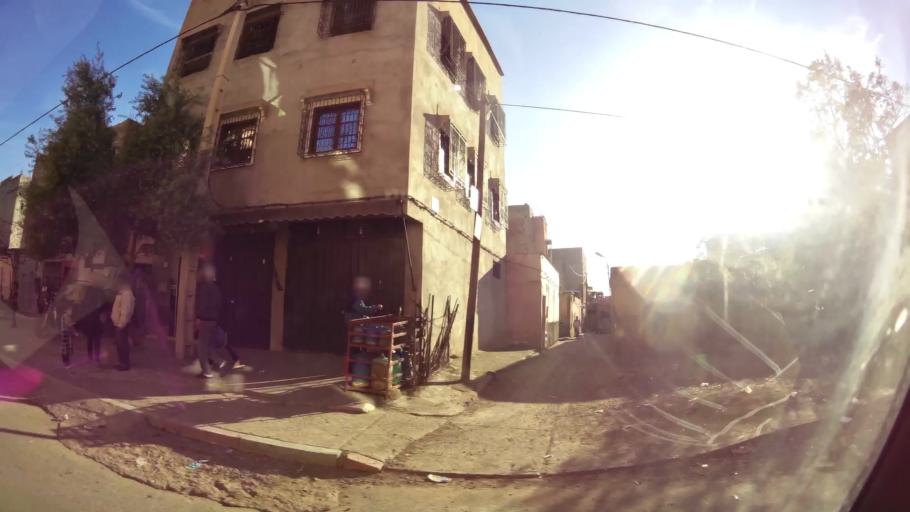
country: MA
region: Marrakech-Tensift-Al Haouz
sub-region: Marrakech
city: Marrakesh
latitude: 31.6178
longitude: -8.0670
